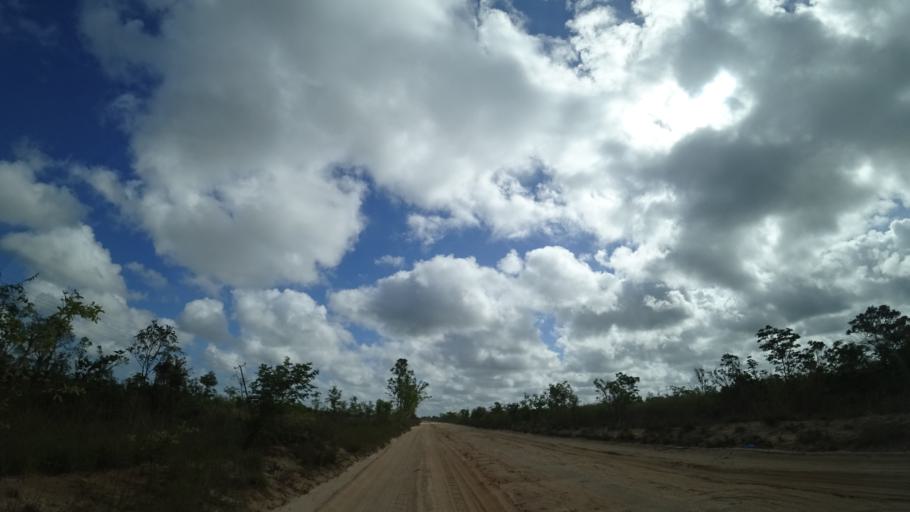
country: MZ
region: Sofala
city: Dondo
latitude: -19.4556
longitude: 34.7187
